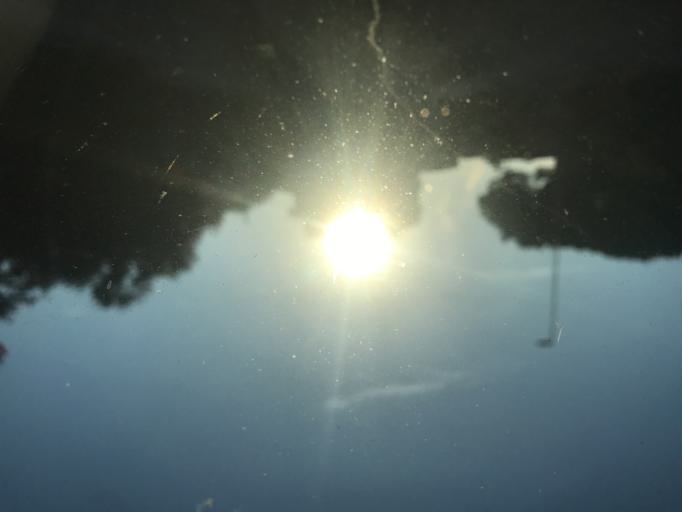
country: IT
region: Sardinia
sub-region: Provincia di Sassari
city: Alghero
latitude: 40.5700
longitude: 8.3272
